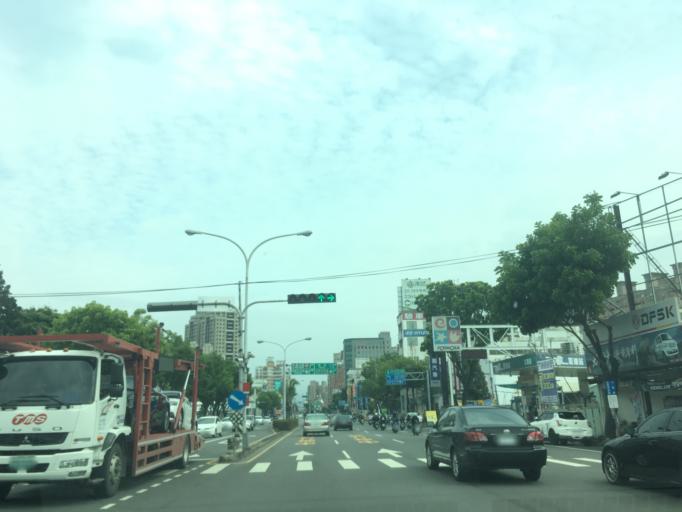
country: TW
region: Taiwan
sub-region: Taichung City
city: Taichung
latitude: 24.1179
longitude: 120.6527
